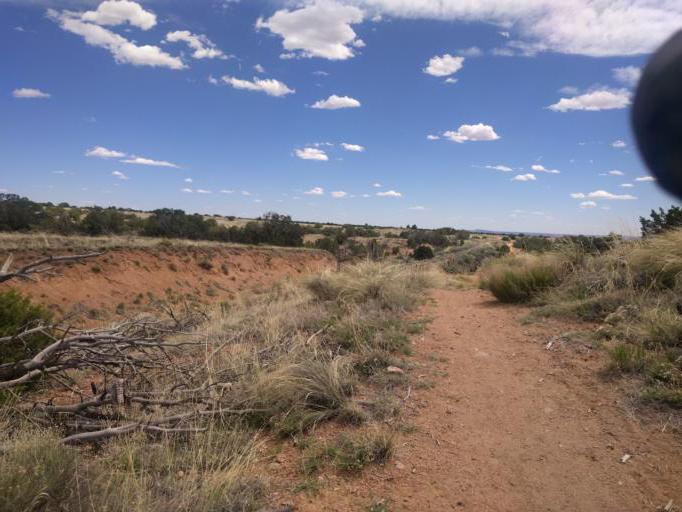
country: US
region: New Mexico
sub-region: Santa Fe County
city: Agua Fria
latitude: 35.6169
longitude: -105.9635
